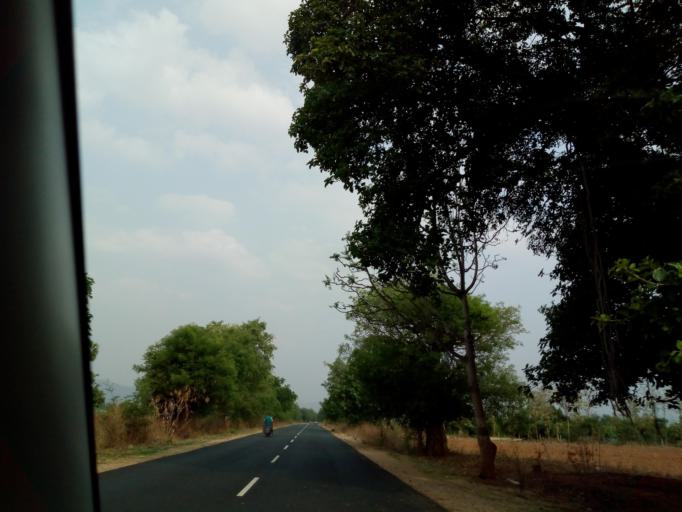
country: IN
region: Andhra Pradesh
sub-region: Prakasam
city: Diguvametta
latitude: 15.3795
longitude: 78.8530
